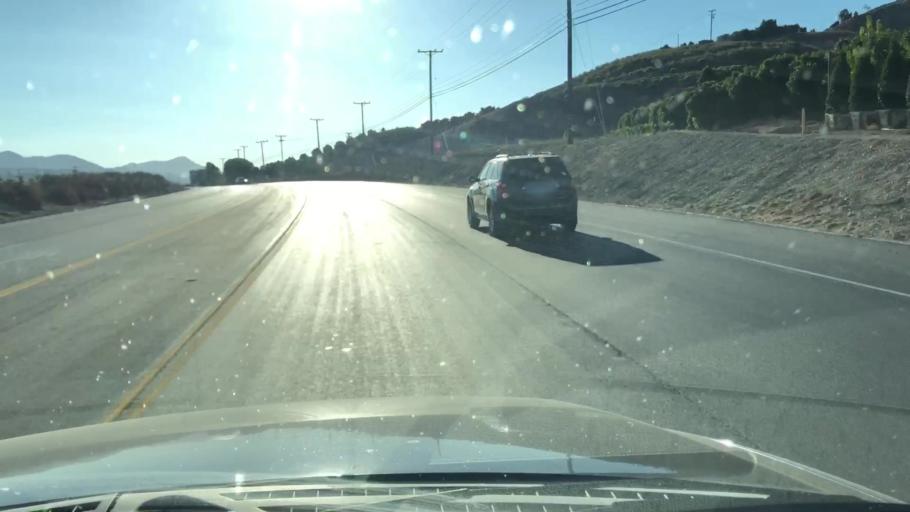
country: US
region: California
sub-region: Ventura County
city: Piru
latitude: 34.4007
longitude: -118.8385
